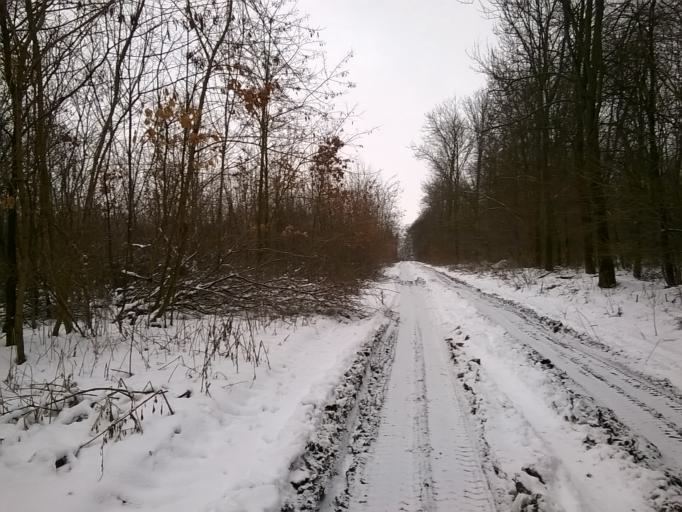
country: SK
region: Nitriansky
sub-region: Okres Nitra
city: Nitra
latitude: 48.2789
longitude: 18.0144
